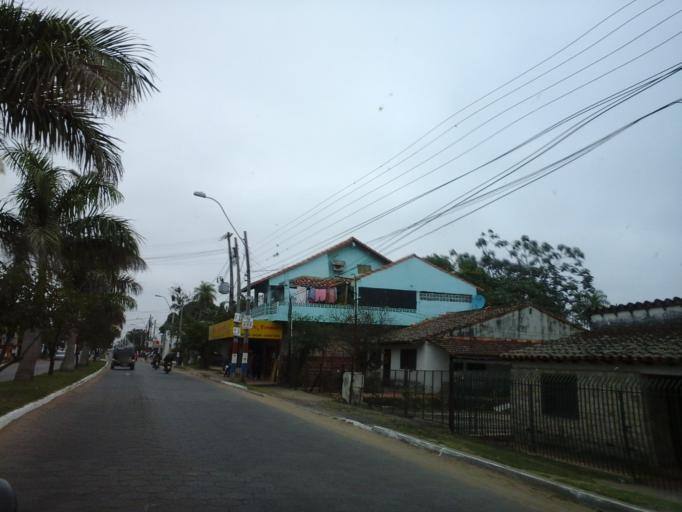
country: PY
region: Neembucu
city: Pilar
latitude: -26.8551
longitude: -58.2970
